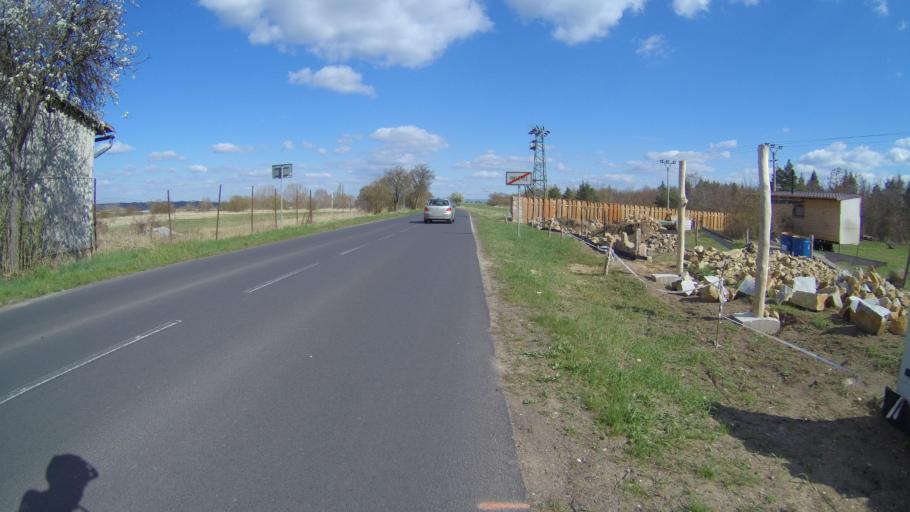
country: CZ
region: Ustecky
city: Brezno
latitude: 50.3480
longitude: 13.4056
